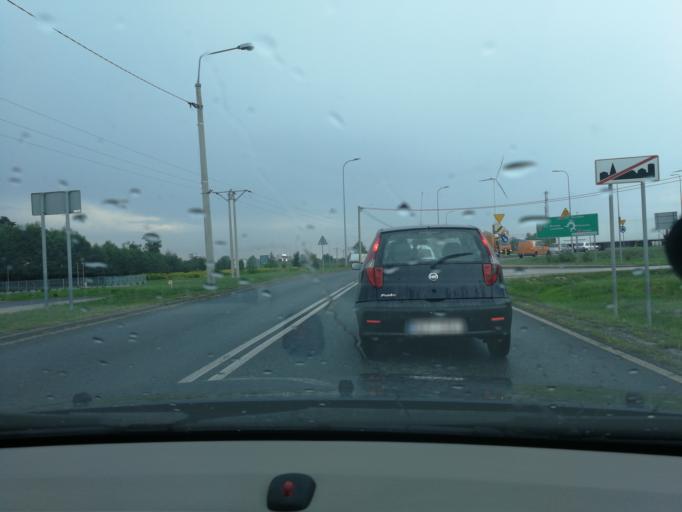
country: PL
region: Masovian Voivodeship
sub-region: Powiat zyrardowski
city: Mszczonow
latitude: 51.9802
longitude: 20.5279
